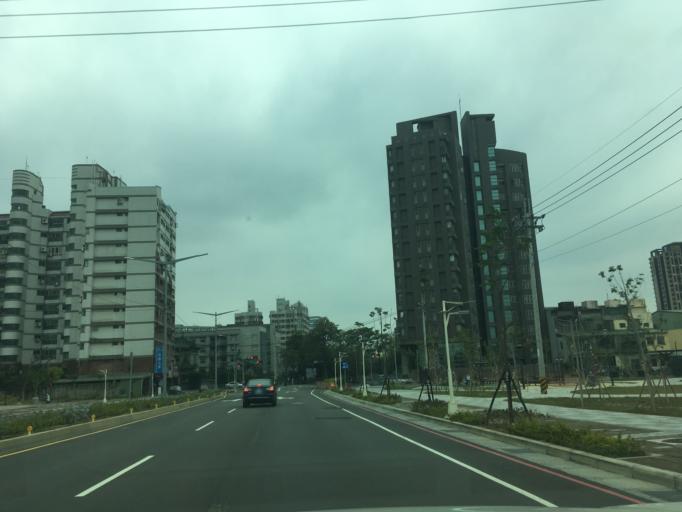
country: TW
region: Taiwan
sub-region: Taichung City
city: Taichung
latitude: 24.1783
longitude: 120.6768
